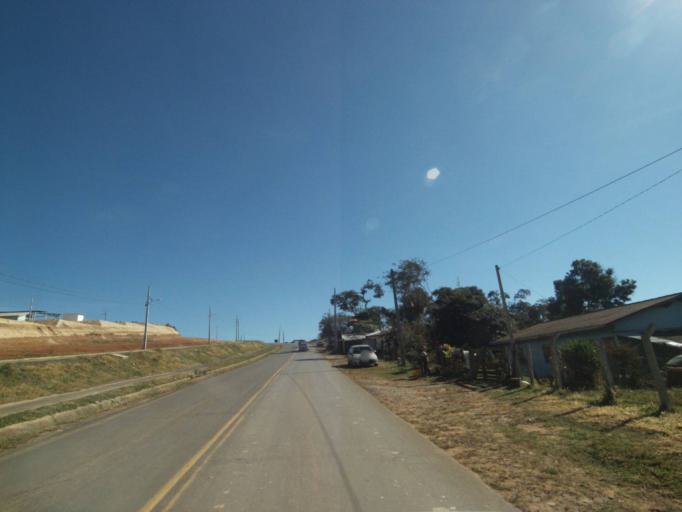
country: BR
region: Parana
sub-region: Tibagi
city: Tibagi
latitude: -24.5191
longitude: -50.4234
